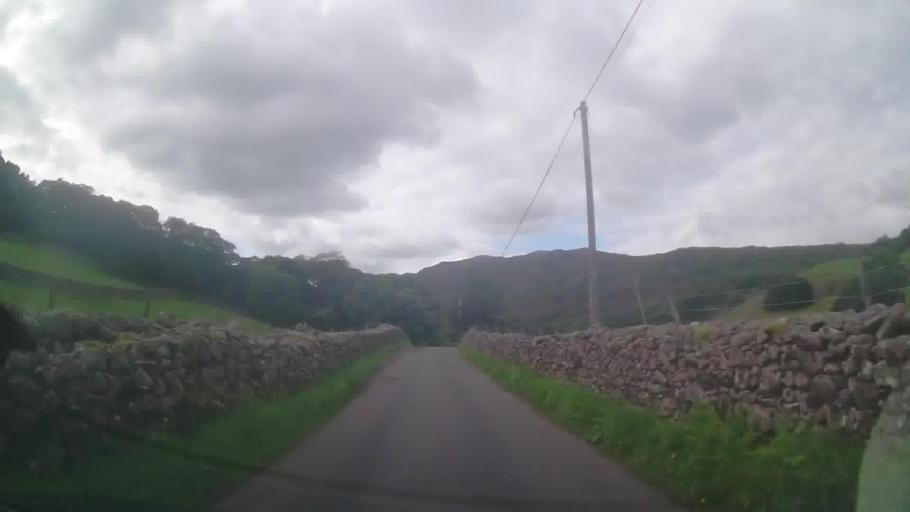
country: GB
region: England
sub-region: Cumbria
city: Millom
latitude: 54.3975
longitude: -3.2614
